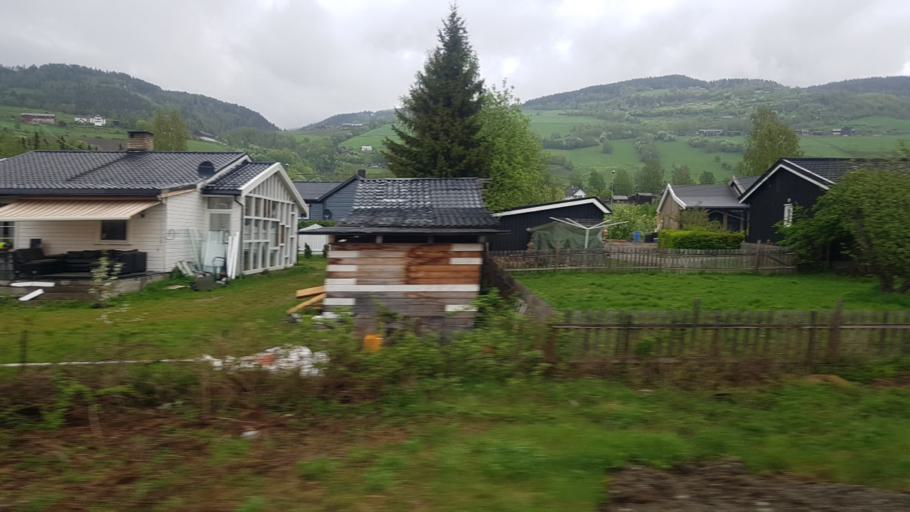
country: NO
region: Oppland
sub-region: Nord-Fron
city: Vinstra
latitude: 61.5856
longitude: 9.7537
